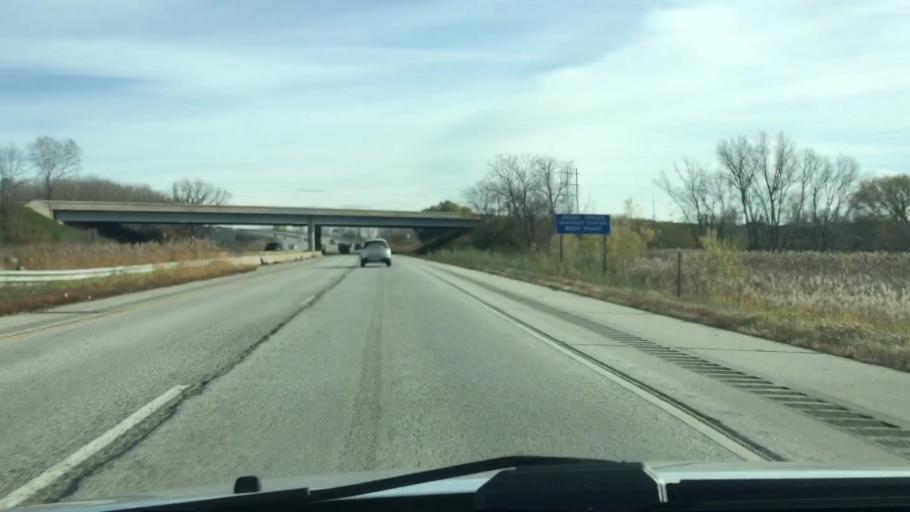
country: US
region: Wisconsin
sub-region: Brown County
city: Green Bay
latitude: 44.5404
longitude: -88.0263
